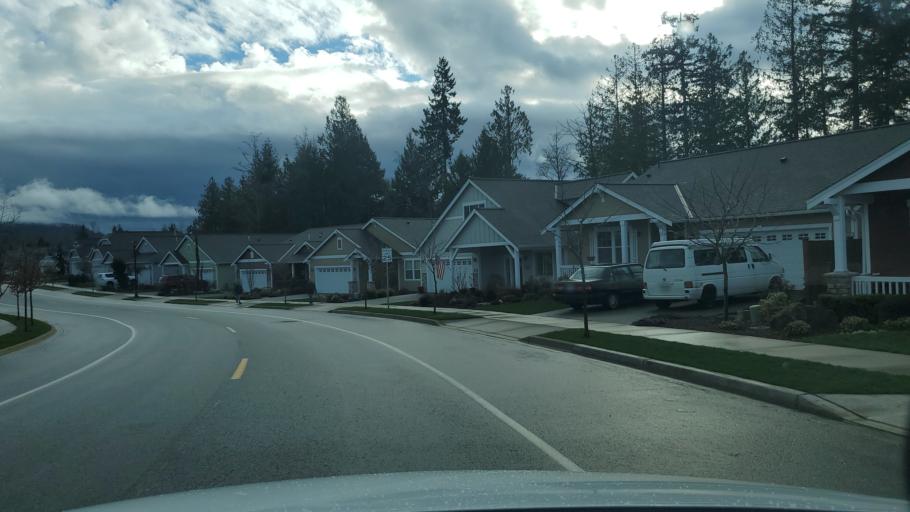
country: US
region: Washington
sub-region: Skagit County
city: Big Lake
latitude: 48.4190
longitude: -122.2798
